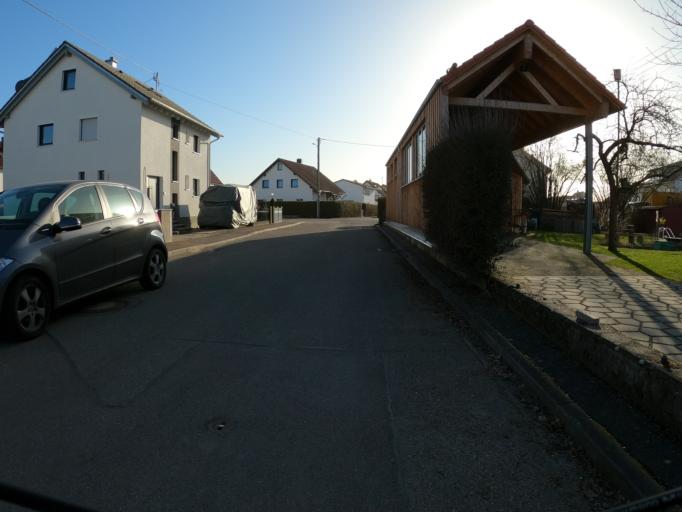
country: DE
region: Bavaria
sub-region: Swabia
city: Holzheim
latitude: 48.4021
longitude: 10.1050
